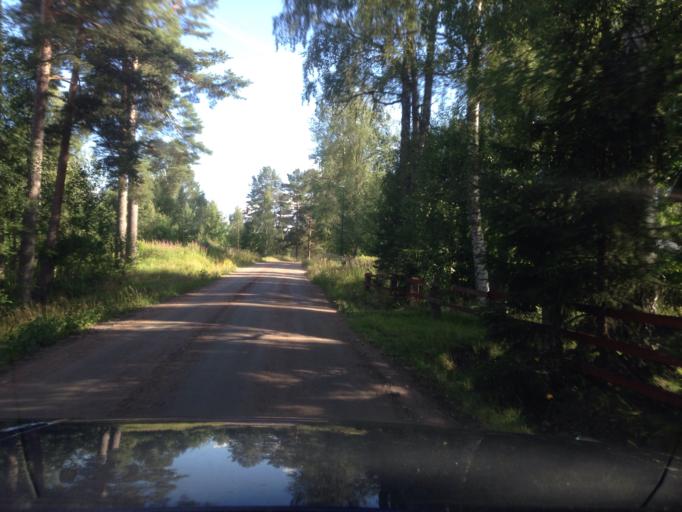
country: SE
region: Dalarna
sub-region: Ludvika Kommun
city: Abborrberget
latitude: 60.2753
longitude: 14.7283
